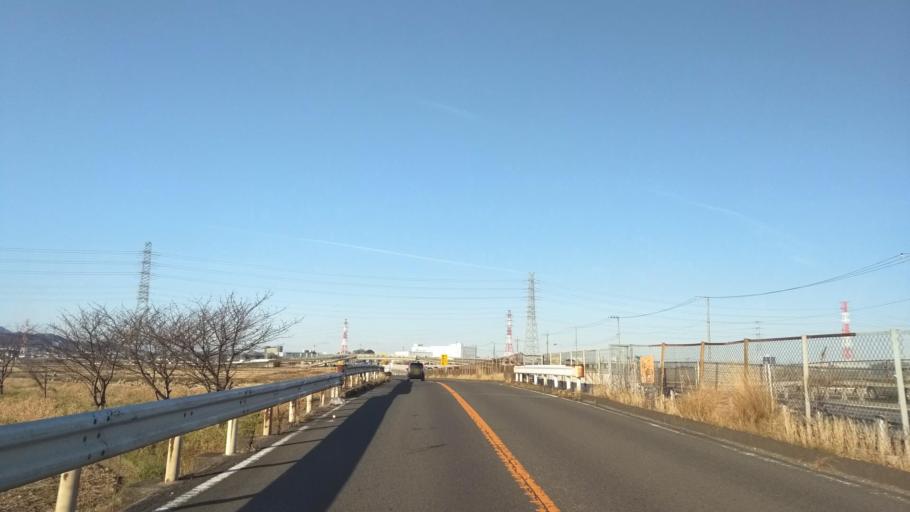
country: JP
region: Kanagawa
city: Isehara
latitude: 35.3942
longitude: 139.3342
